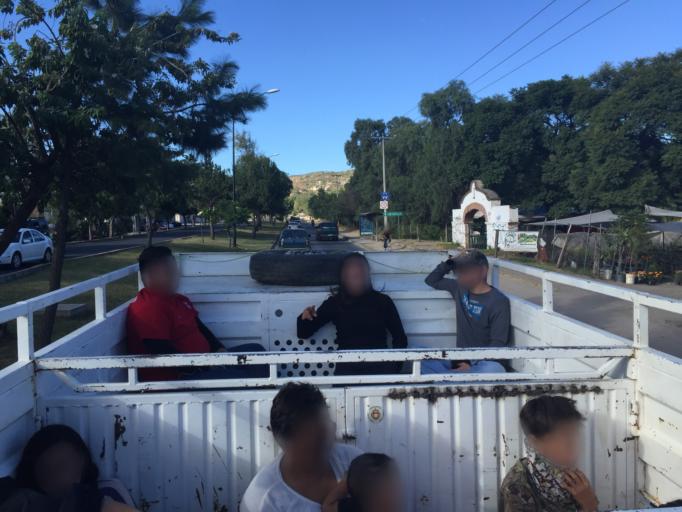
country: MX
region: Guanajuato
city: Leon
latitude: 21.1819
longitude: -101.6640
